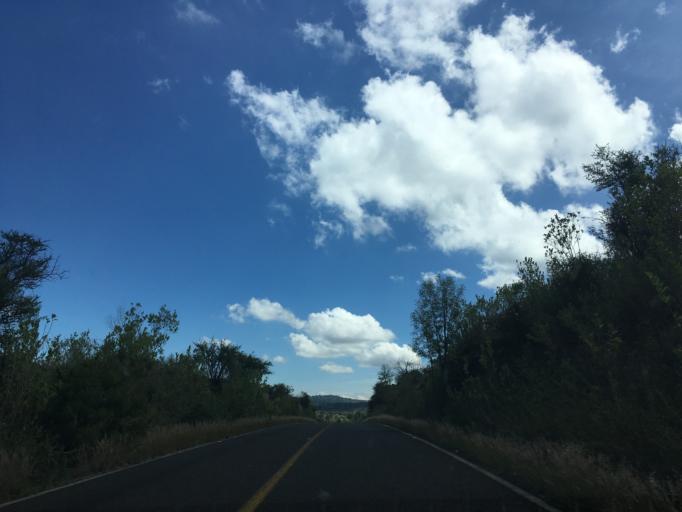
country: MX
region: Michoacan
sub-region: Morelia
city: Cuto de la Esperanza
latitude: 19.7813
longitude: -101.4116
